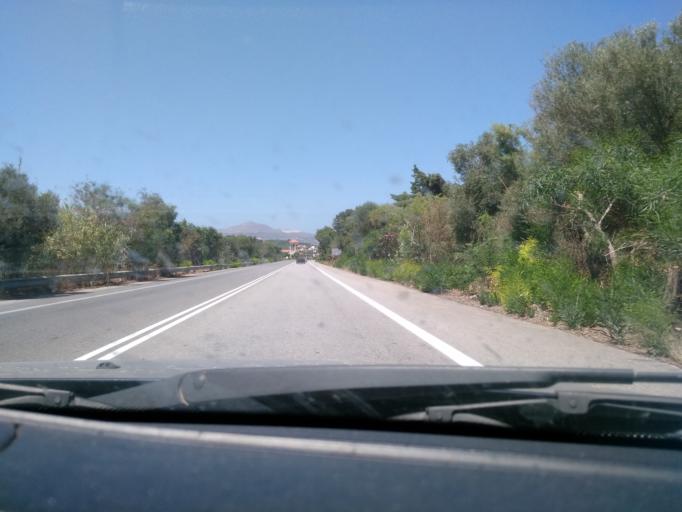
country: GR
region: Crete
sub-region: Nomos Chanias
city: Kalivai
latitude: 35.4352
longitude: 24.1662
